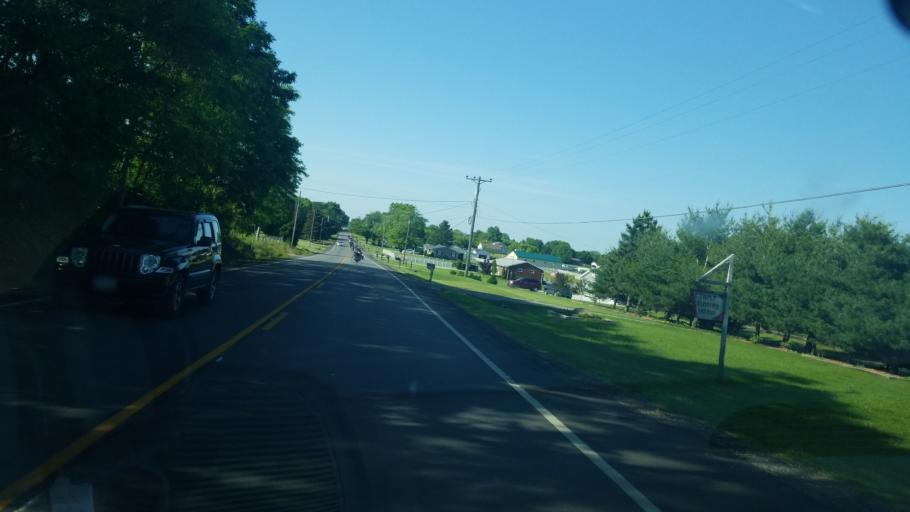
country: US
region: Ohio
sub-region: Wayne County
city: Smithville
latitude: 40.8957
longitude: -81.9158
